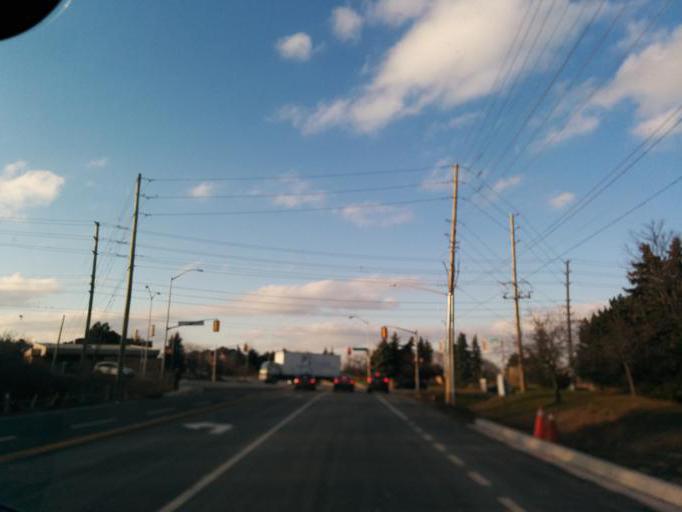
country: CA
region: Ontario
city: Oakville
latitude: 43.4919
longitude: -79.6818
